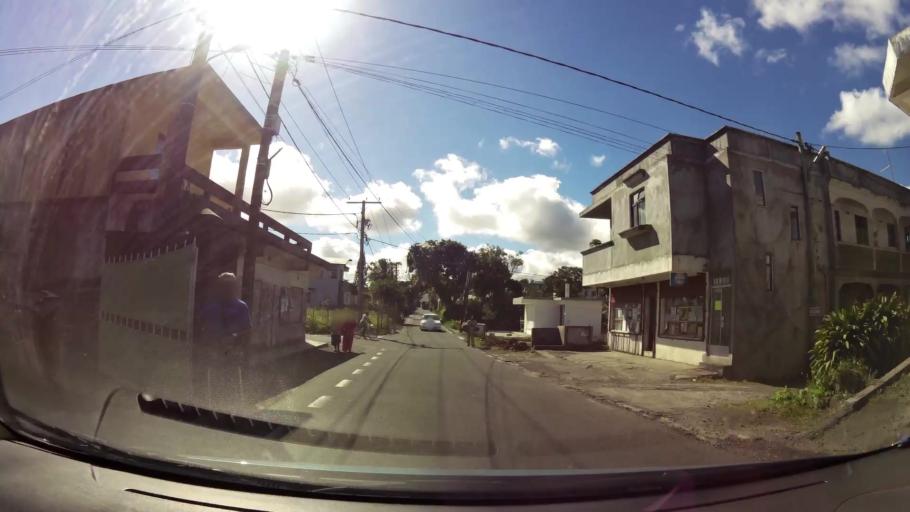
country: MU
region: Plaines Wilhems
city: Vacoas
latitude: -20.3030
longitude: 57.5001
